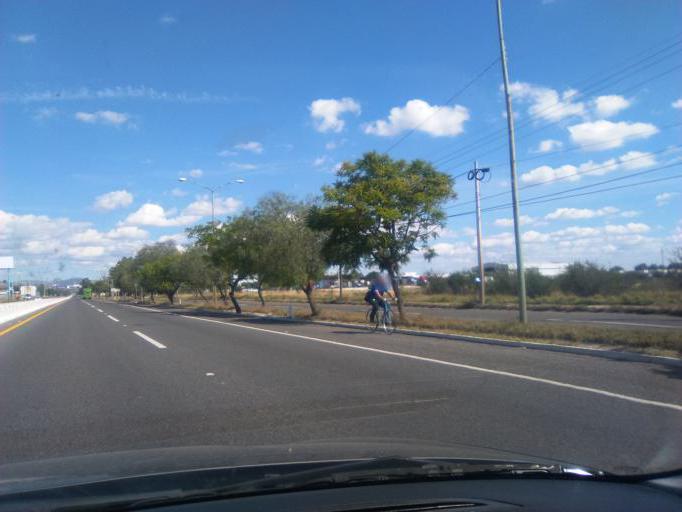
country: MX
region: Guanajuato
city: Silao
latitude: 20.9484
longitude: -101.4008
